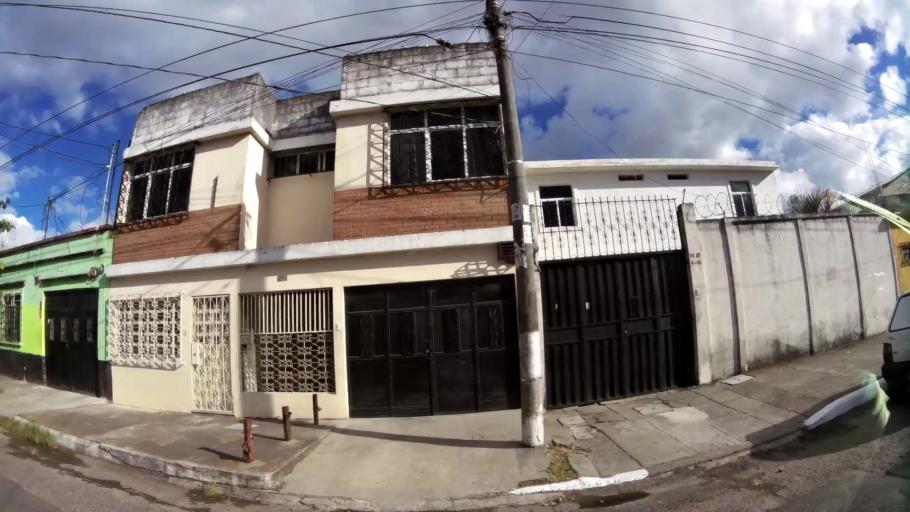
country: GT
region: Guatemala
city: Guatemala City
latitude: 14.6189
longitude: -90.5479
